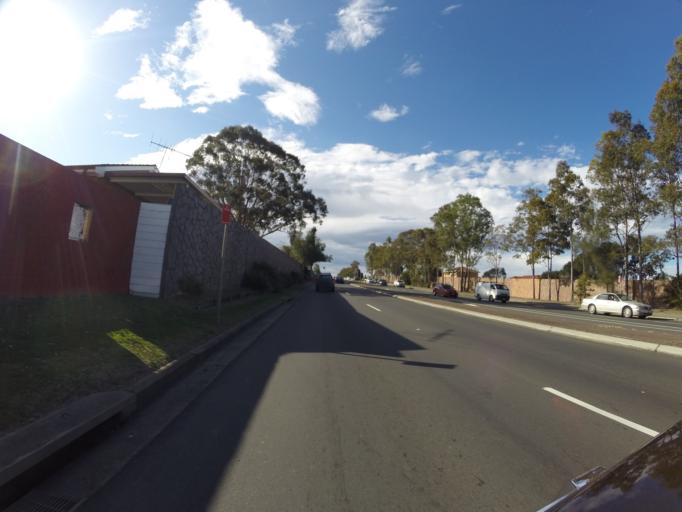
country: AU
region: New South Wales
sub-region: Fairfield
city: Cecil Park
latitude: -33.8790
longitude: 150.8669
